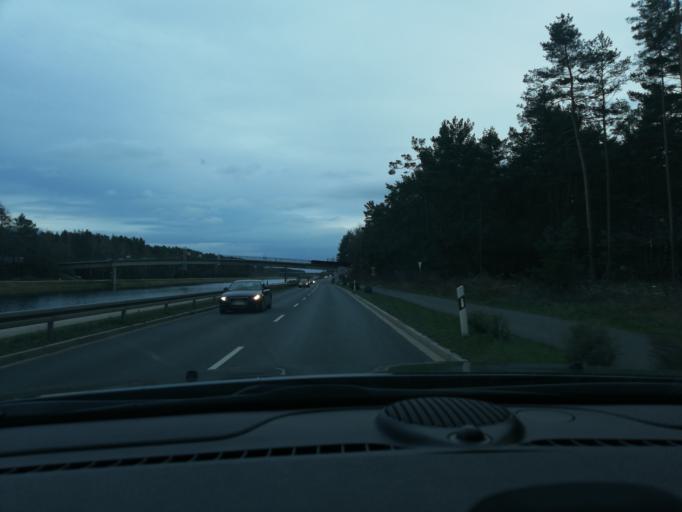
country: DE
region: Bavaria
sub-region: Regierungsbezirk Mittelfranken
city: Mohrendorf
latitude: 49.6098
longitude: 10.9719
